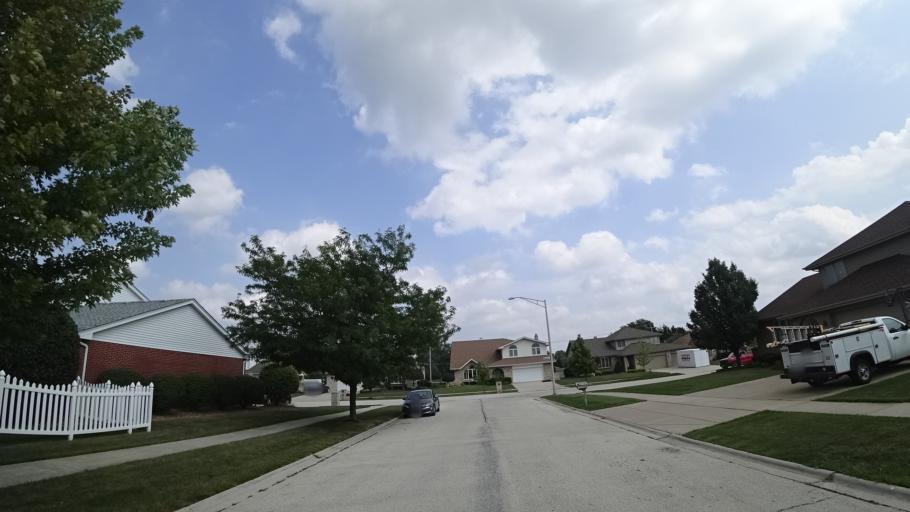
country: US
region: Illinois
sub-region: Will County
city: Goodings Grove
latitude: 41.6356
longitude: -87.8938
